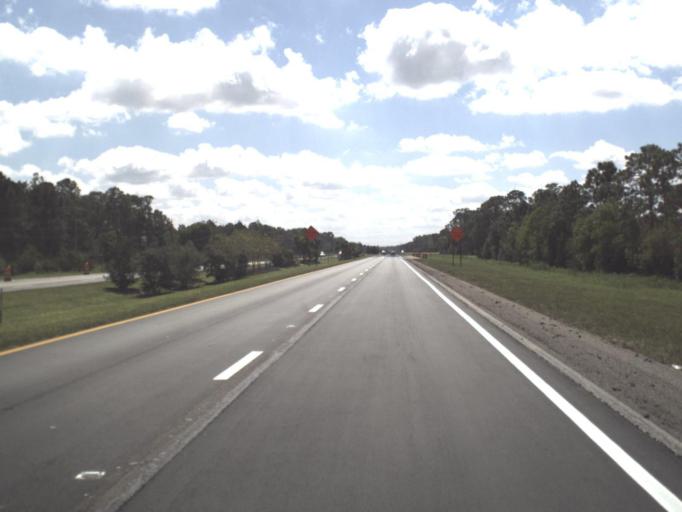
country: US
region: Florida
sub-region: Lee County
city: Suncoast Estates
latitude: 26.7581
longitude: -81.9248
